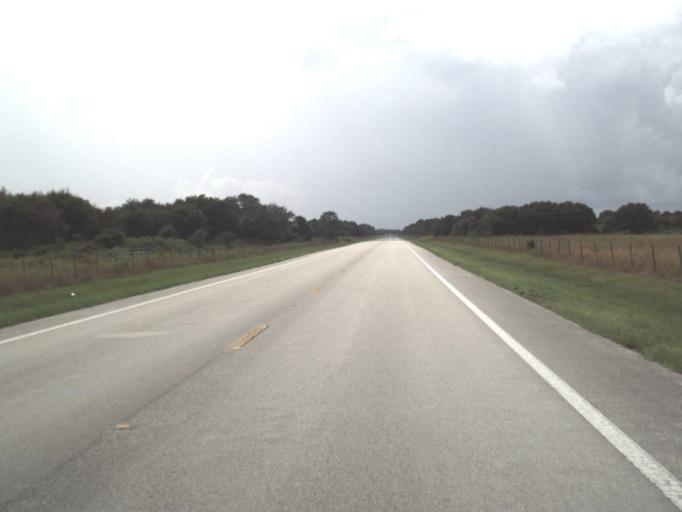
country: US
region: Florida
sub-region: Sarasota County
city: Warm Mineral Springs
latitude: 27.1935
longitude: -82.1741
